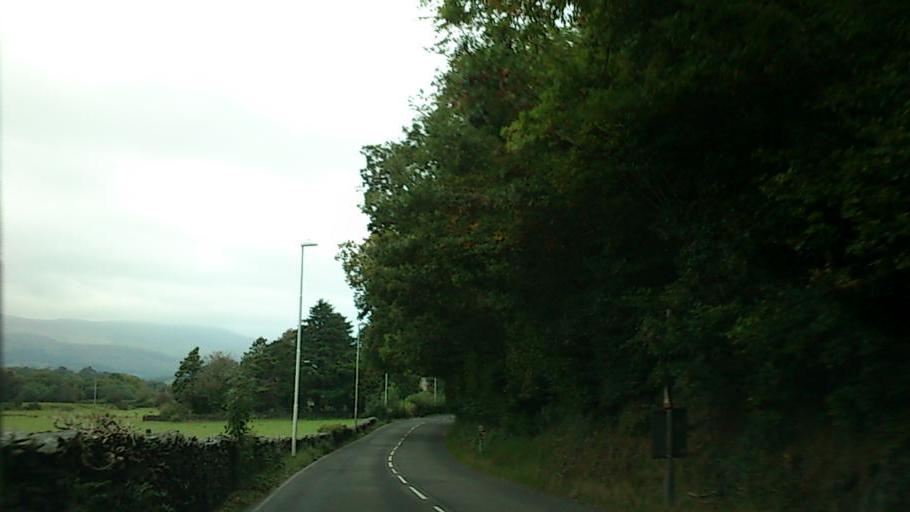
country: GB
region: Wales
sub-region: Sir Powys
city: Machynlleth
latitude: 52.5396
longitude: -3.9397
